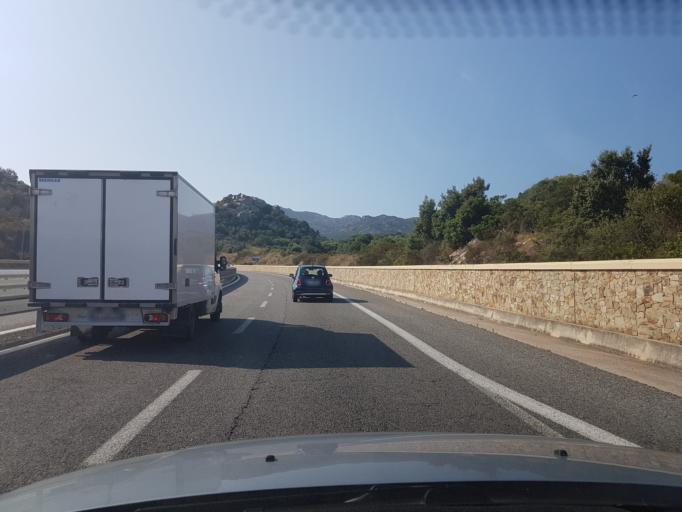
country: IT
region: Sardinia
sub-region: Provincia di Olbia-Tempio
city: Padru
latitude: 40.8016
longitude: 9.5910
